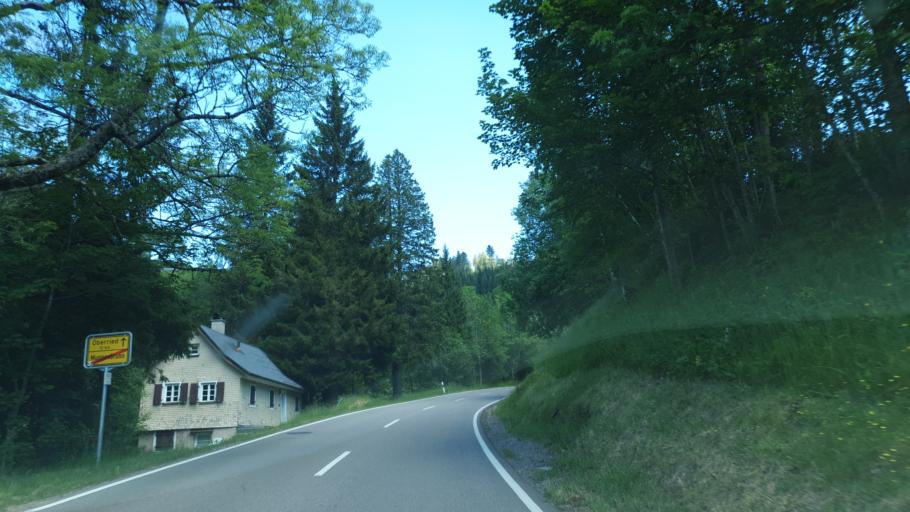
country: DE
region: Baden-Wuerttemberg
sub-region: Freiburg Region
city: Todtnau
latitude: 47.8596
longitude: 7.9183
